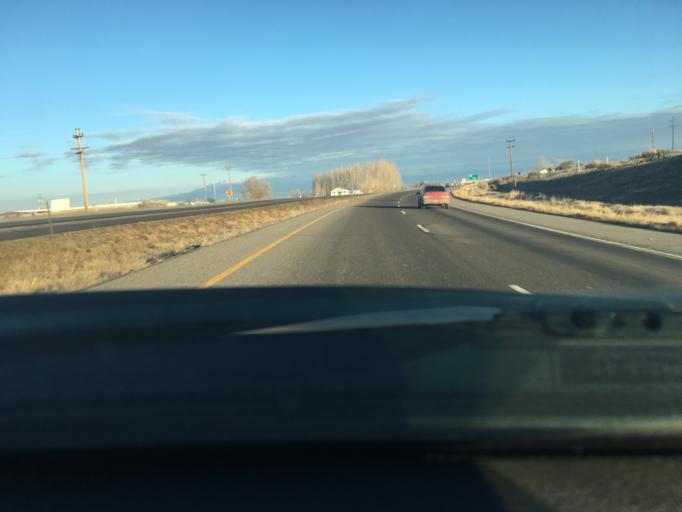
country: US
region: Colorado
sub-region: Montrose County
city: Olathe
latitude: 38.5955
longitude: -107.9725
